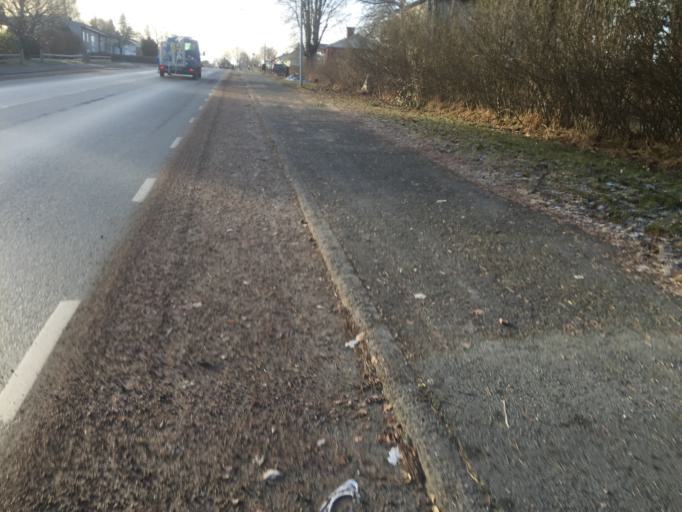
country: SE
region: Joenkoeping
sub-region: Aneby Kommun
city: Aneby
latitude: 57.8445
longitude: 14.8195
